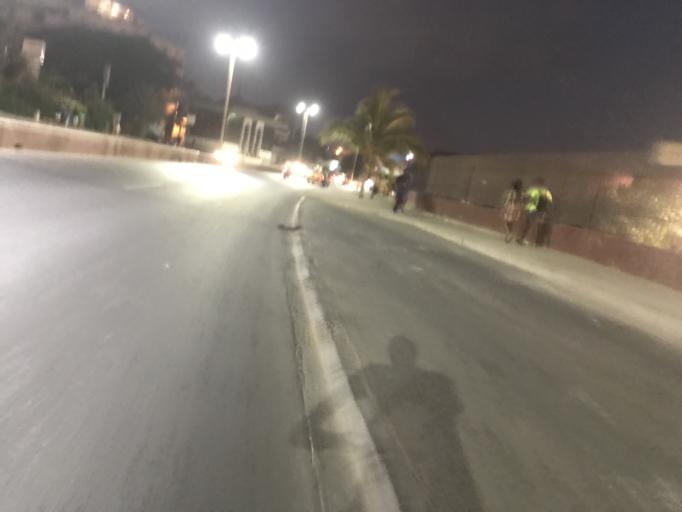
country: SN
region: Dakar
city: Dakar
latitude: 14.6790
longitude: -17.4622
